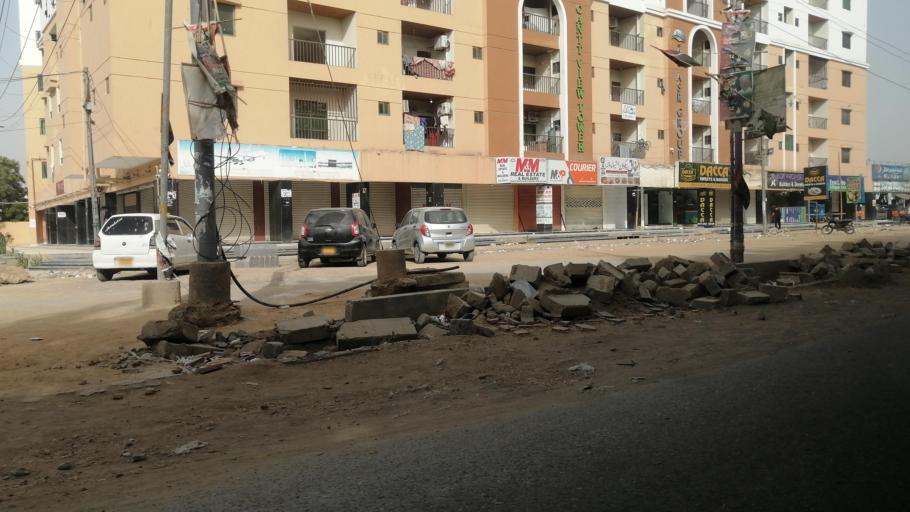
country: PK
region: Sindh
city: Malir Cantonment
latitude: 24.9288
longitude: 67.1789
